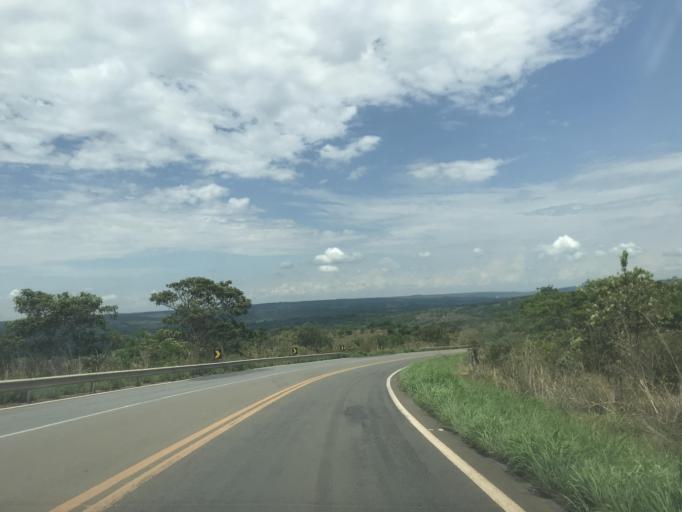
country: BR
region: Goias
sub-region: Luziania
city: Luziania
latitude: -16.3517
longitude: -48.0429
